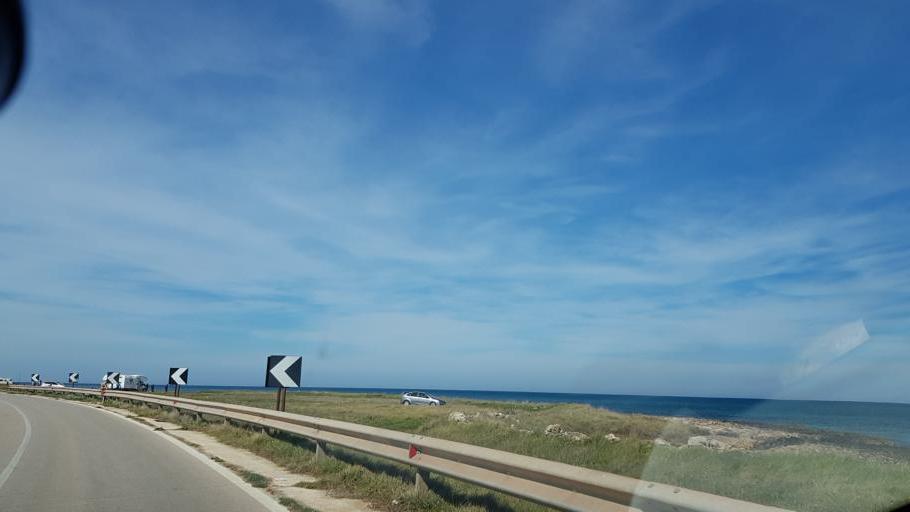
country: IT
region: Apulia
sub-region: Provincia di Brindisi
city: Pezze di Greco
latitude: 40.8506
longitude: 17.4517
